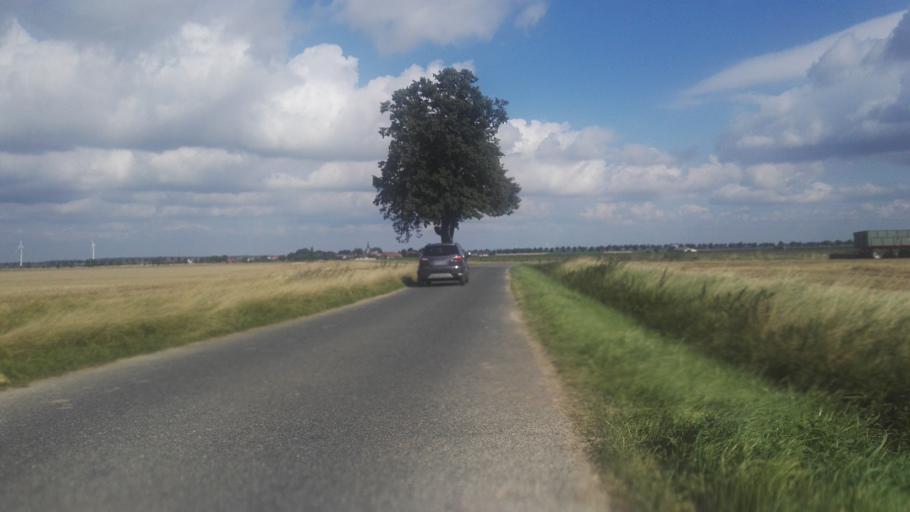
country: DE
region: Lower Saxony
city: Schellerten
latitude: 52.1574
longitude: 10.0523
